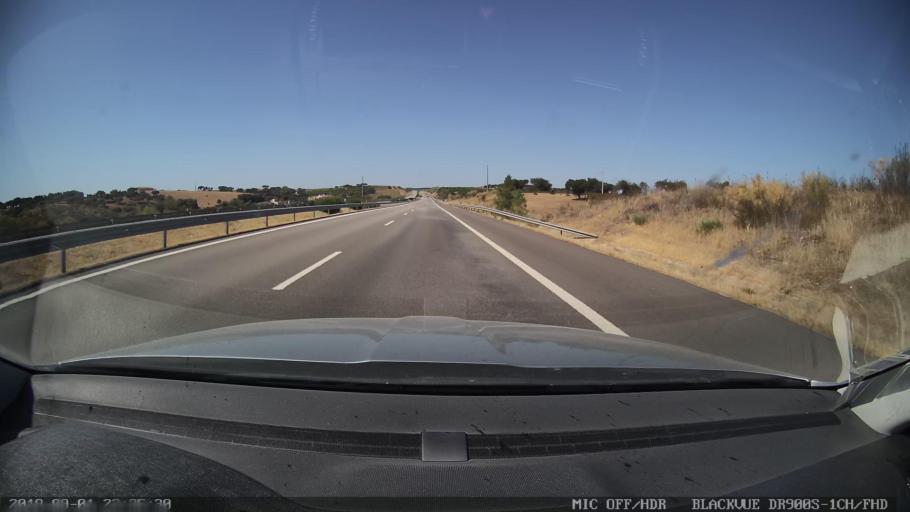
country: PT
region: Evora
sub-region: Vila Vicosa
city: Vila Vicosa
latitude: 38.8437
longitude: -7.3921
